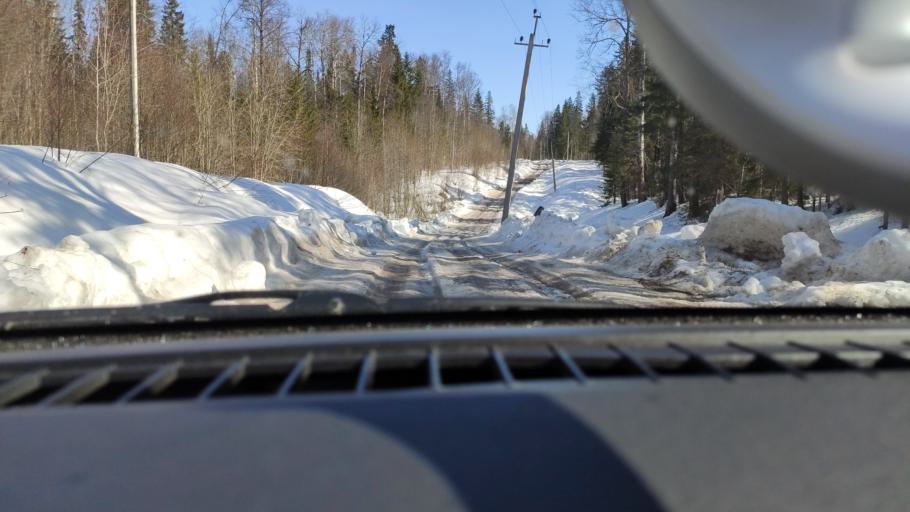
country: RU
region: Perm
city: Perm
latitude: 58.2201
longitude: 56.1612
